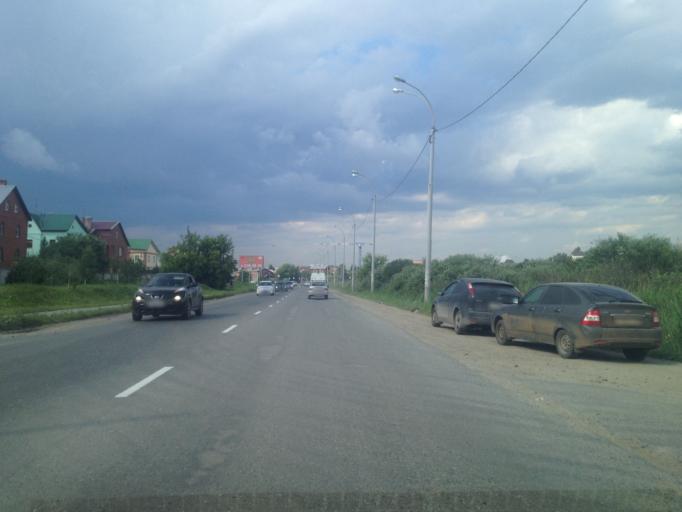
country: RU
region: Sverdlovsk
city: Shirokaya Rechka
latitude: 56.8020
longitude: 60.4942
